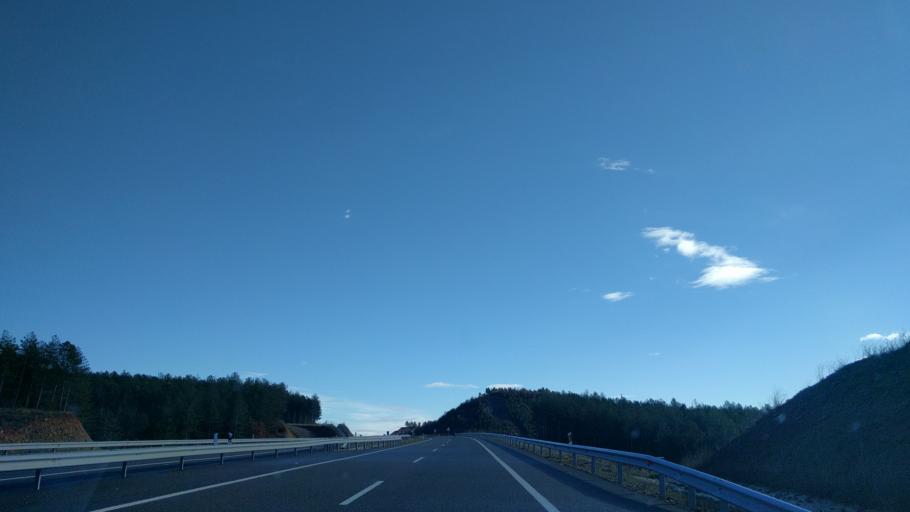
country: ES
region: Aragon
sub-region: Provincia de Zaragoza
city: Undues de Lerda
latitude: 42.6231
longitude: -1.1302
